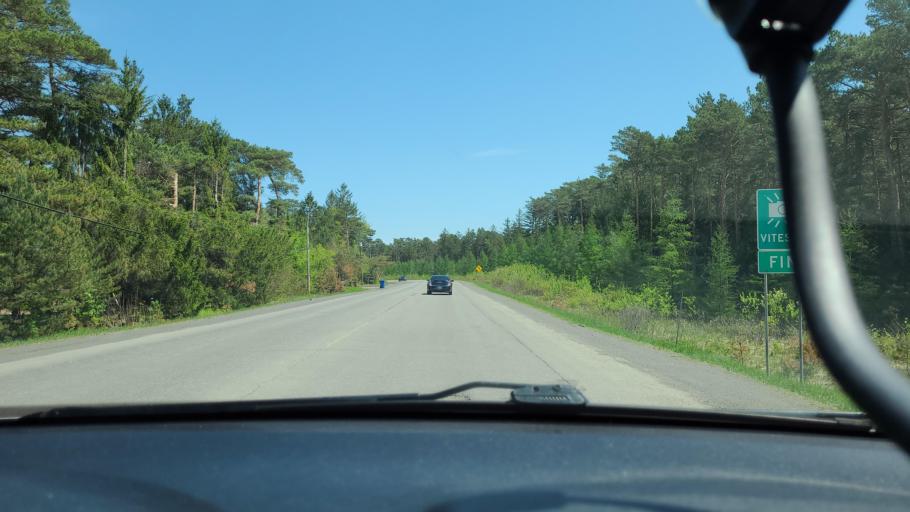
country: CA
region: Quebec
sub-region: Laurentides
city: Lachute
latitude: 45.6637
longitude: -74.2554
